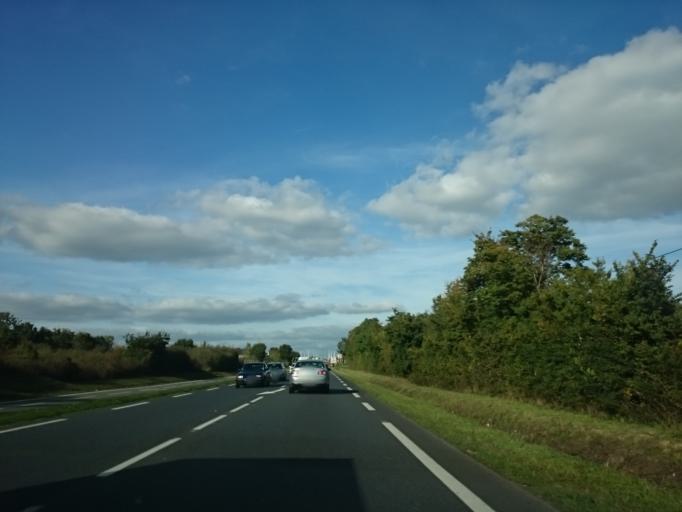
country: FR
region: Pays de la Loire
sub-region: Departement de la Loire-Atlantique
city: Saint-Herblain
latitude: 47.2232
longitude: -1.6534
